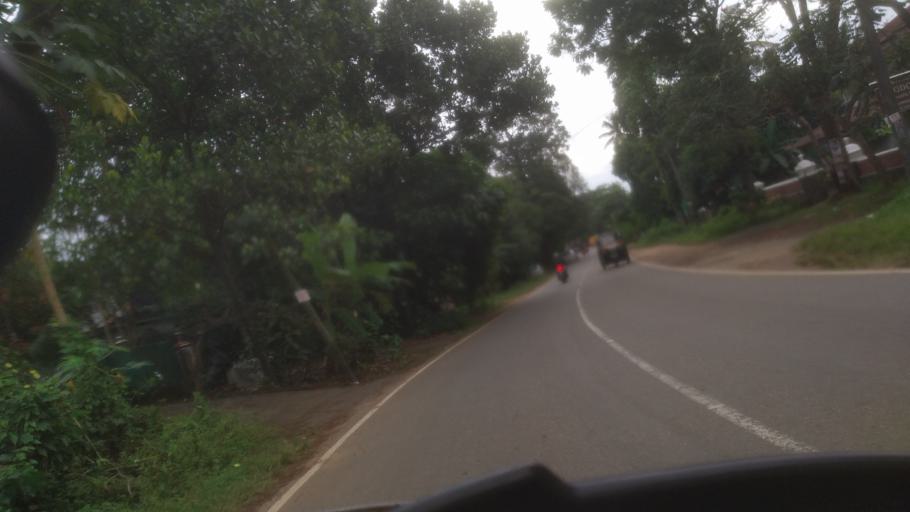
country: IN
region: Kerala
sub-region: Idukki
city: Munnar
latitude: 9.9988
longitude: 76.9715
